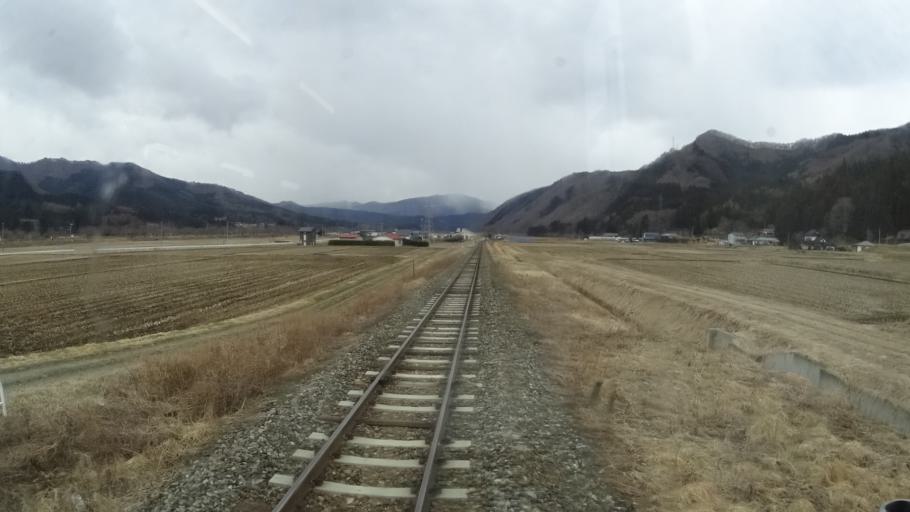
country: JP
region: Iwate
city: Tono
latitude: 39.3112
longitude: 141.4328
